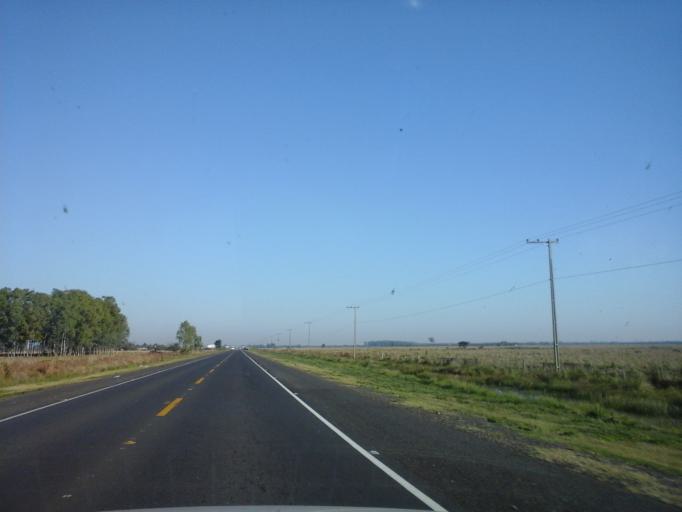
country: PY
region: Neembucu
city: Pilar
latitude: -26.8458
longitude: -58.2528
